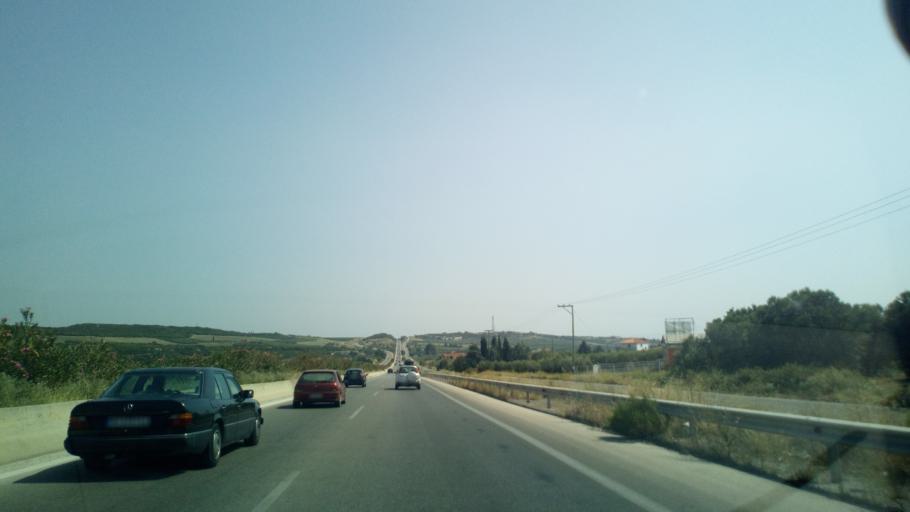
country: GR
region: Central Macedonia
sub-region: Nomos Chalkidikis
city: Nea Kallikrateia
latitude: 40.3471
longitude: 23.0627
